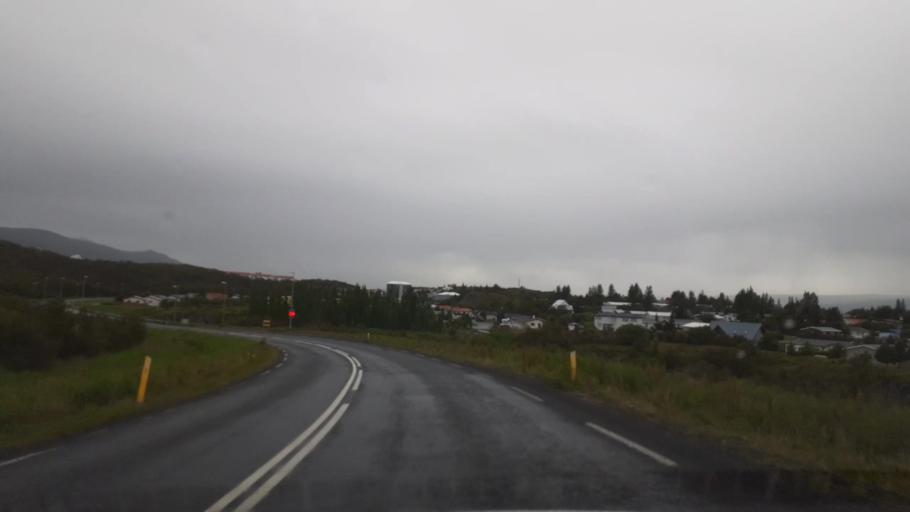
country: IS
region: East
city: Egilsstadir
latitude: 65.2672
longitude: -14.3789
